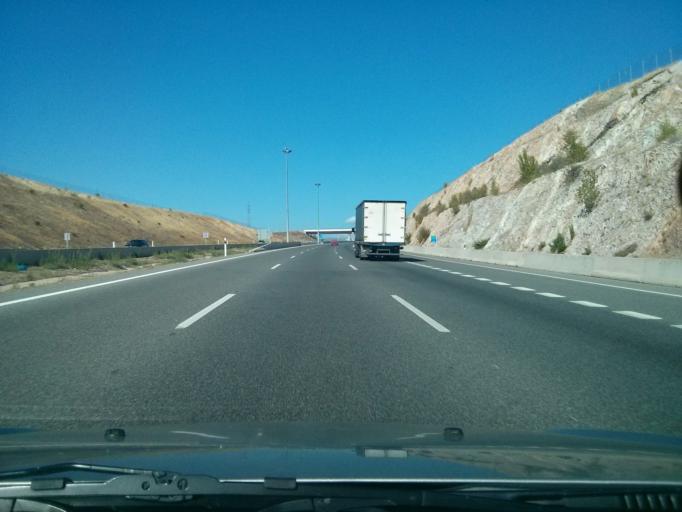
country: ES
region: Madrid
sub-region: Provincia de Madrid
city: Pedrezuela
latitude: 40.7516
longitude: -3.5897
